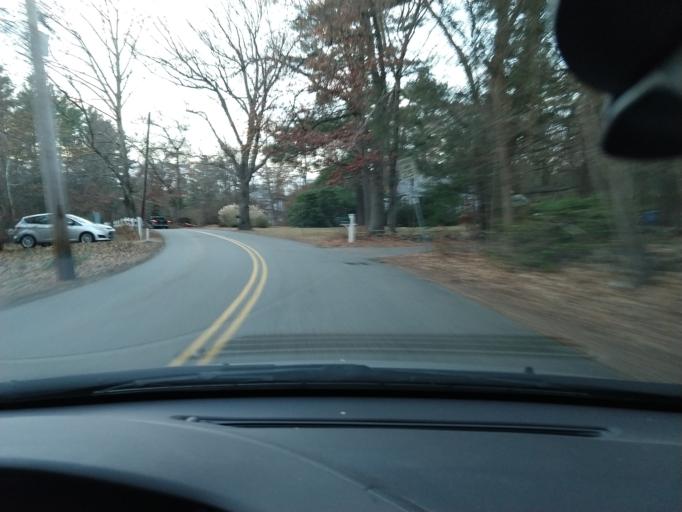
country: US
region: Massachusetts
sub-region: Middlesex County
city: Bedford
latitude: 42.4886
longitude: -71.2443
